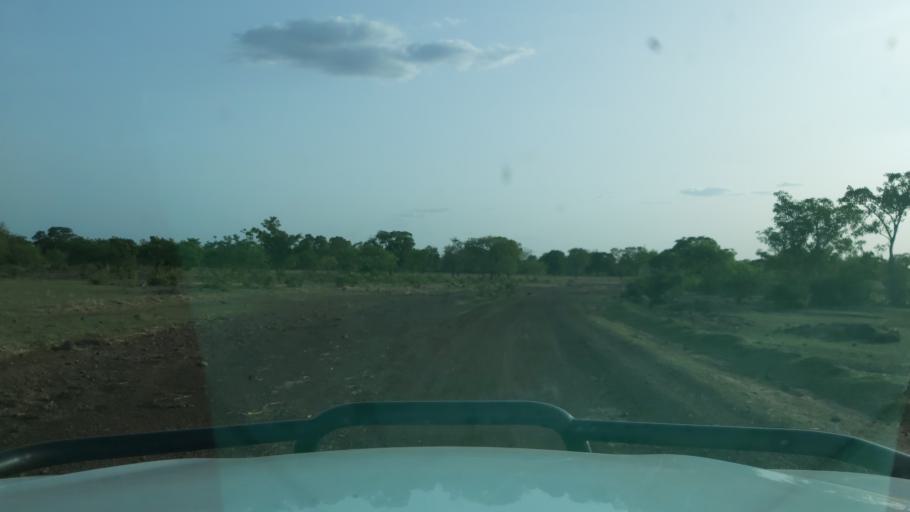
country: ML
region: Koulikoro
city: Kolokani
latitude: 13.2067
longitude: -7.9146
